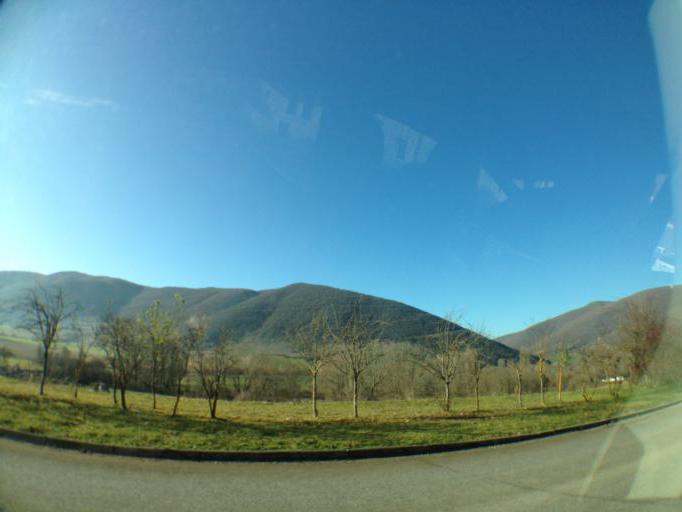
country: IT
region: Umbria
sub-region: Provincia di Perugia
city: Norcia
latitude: 42.7909
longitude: 13.0923
